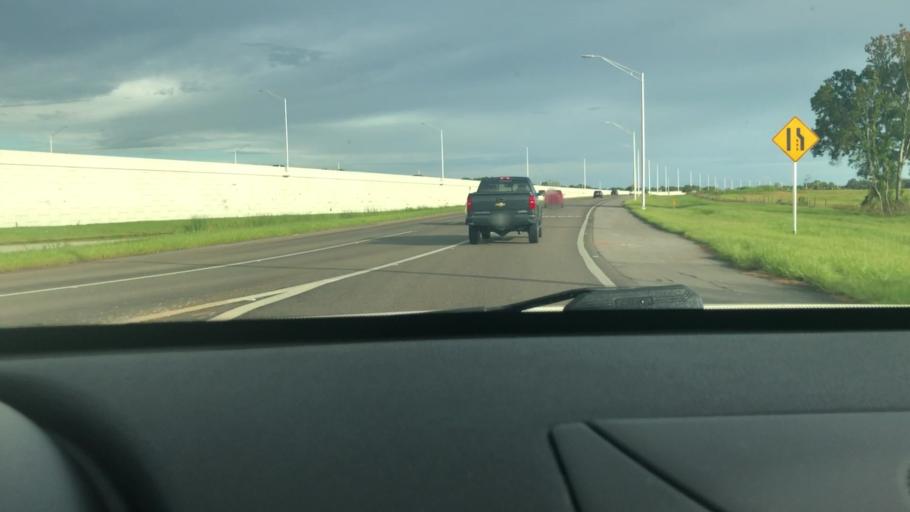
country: US
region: Florida
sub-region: Sarasota County
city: The Meadows
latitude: 27.3879
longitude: -82.4499
